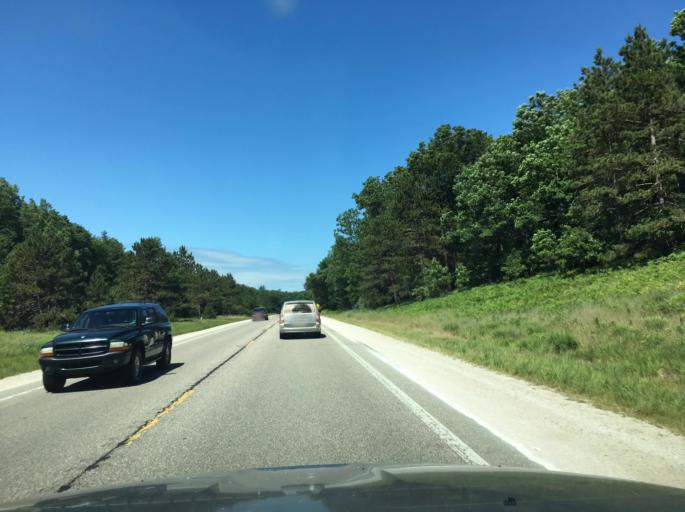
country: US
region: Michigan
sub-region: Osceola County
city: Reed City
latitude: 43.8926
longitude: -85.6736
